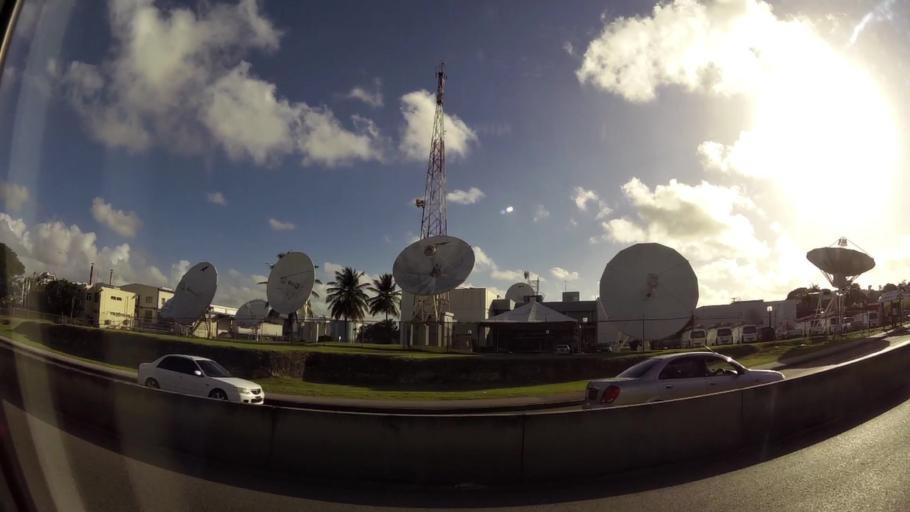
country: BB
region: Saint Michael
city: Bridgetown
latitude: 13.0983
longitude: -59.5800
